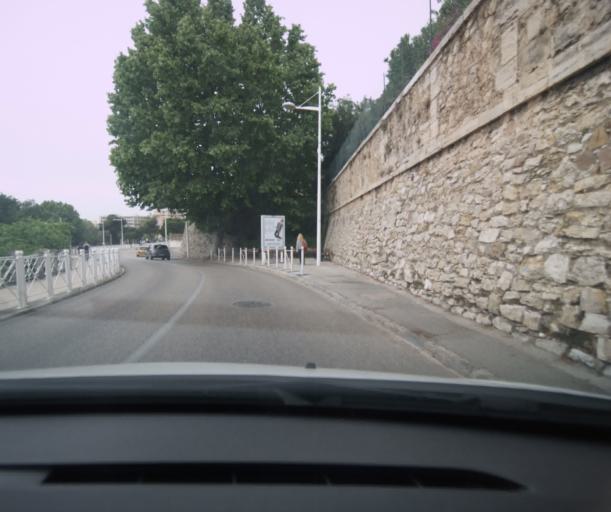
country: FR
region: Provence-Alpes-Cote d'Azur
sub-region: Departement du Var
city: Toulon
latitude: 43.1087
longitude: 5.9439
